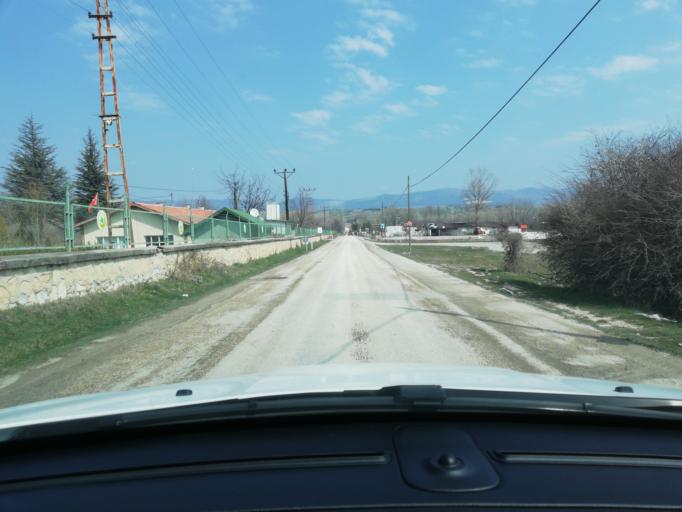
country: TR
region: Kastamonu
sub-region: Cide
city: Kastamonu
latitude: 41.4486
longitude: 33.7655
